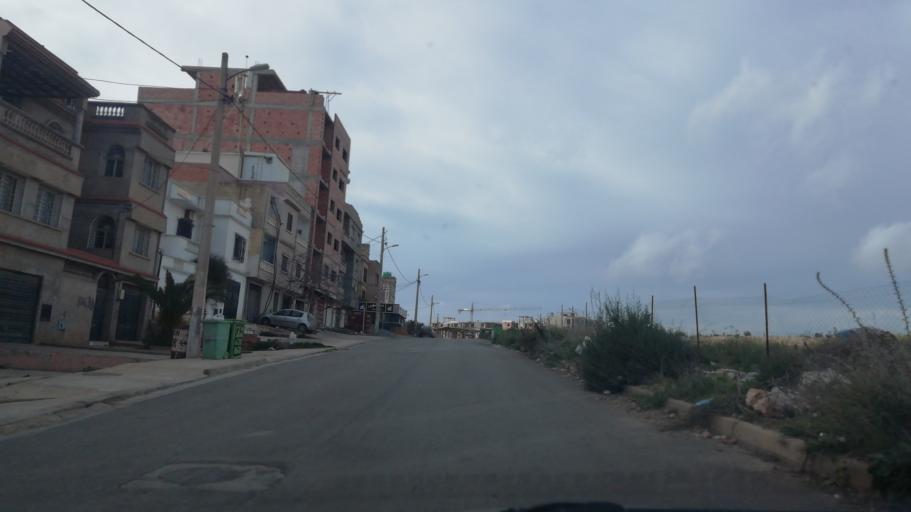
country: DZ
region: Oran
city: Bir el Djir
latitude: 35.7305
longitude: -0.5684
